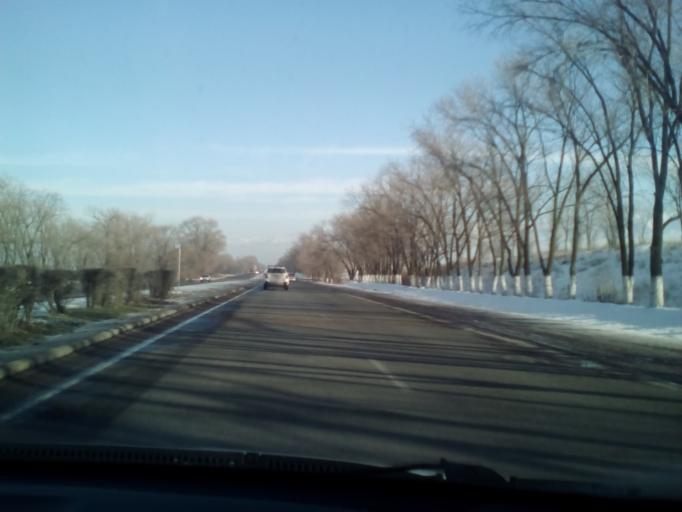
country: KZ
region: Almaty Oblysy
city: Burunday
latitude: 43.2208
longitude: 76.4534
